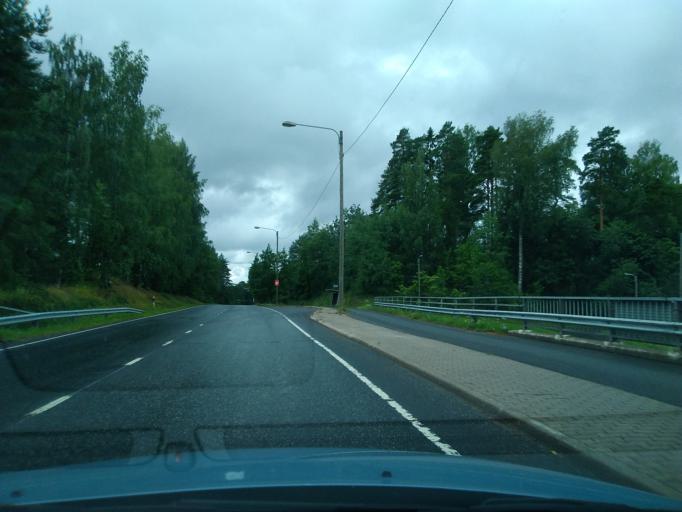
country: FI
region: Haeme
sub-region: Forssa
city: Tammela
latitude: 60.8073
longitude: 23.7802
